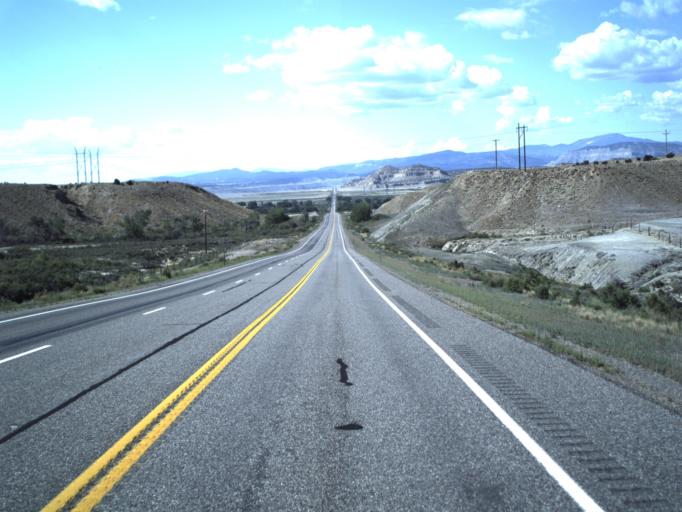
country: US
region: Utah
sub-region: Emery County
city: Ferron
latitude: 38.8900
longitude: -111.2818
